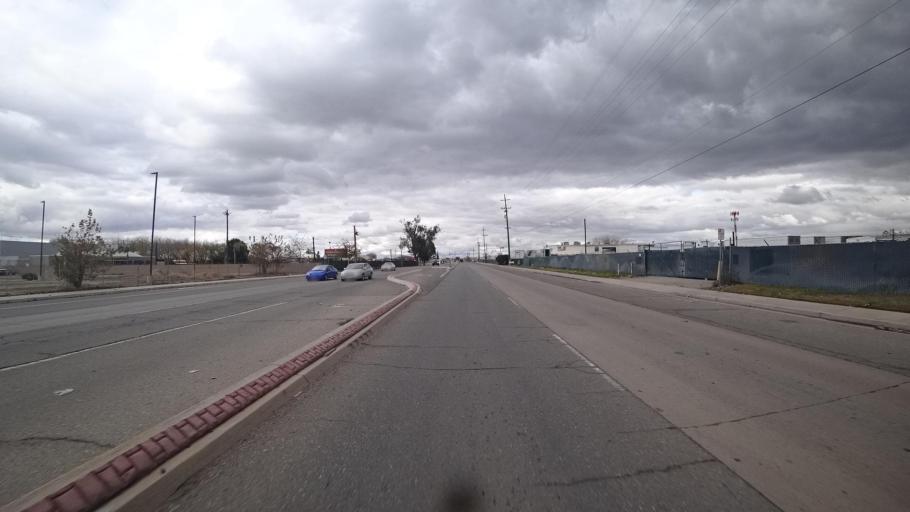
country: US
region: California
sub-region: Kern County
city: Greenfield
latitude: 35.3220
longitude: -119.0031
